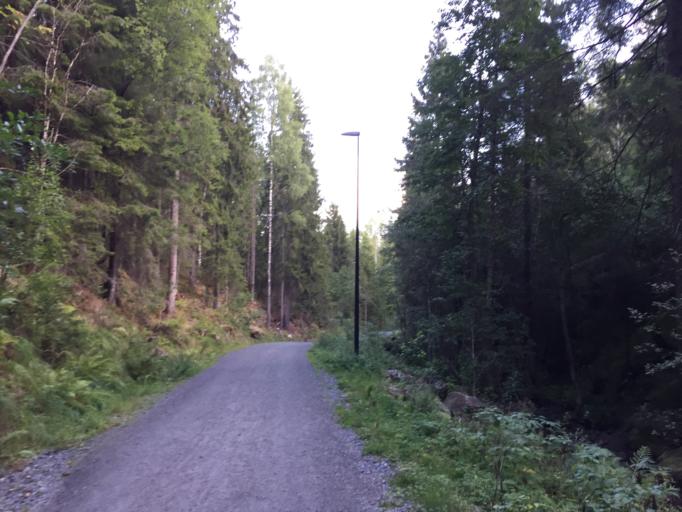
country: NO
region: Akershus
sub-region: Skedsmo
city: Lillestrom
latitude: 59.9279
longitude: 11.0286
